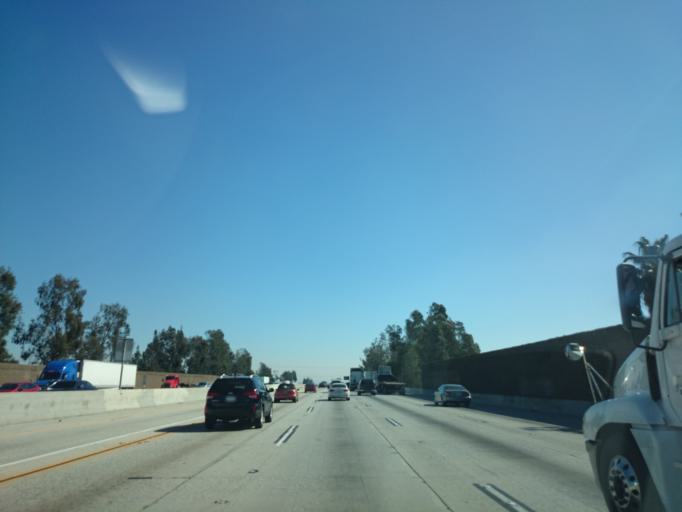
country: US
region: California
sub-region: San Bernardino County
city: Upland
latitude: 34.0821
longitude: -117.6312
